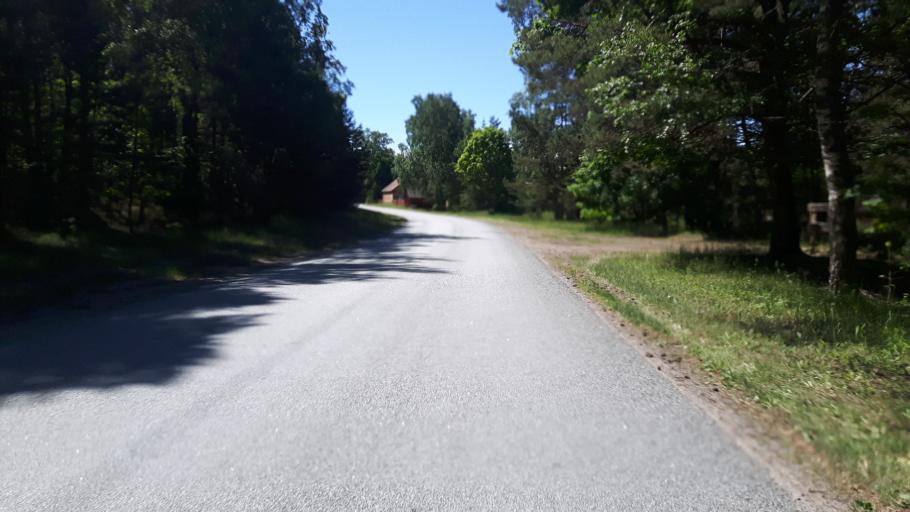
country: LV
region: Salacgrivas
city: Ainazi
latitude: 58.0391
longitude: 24.4652
